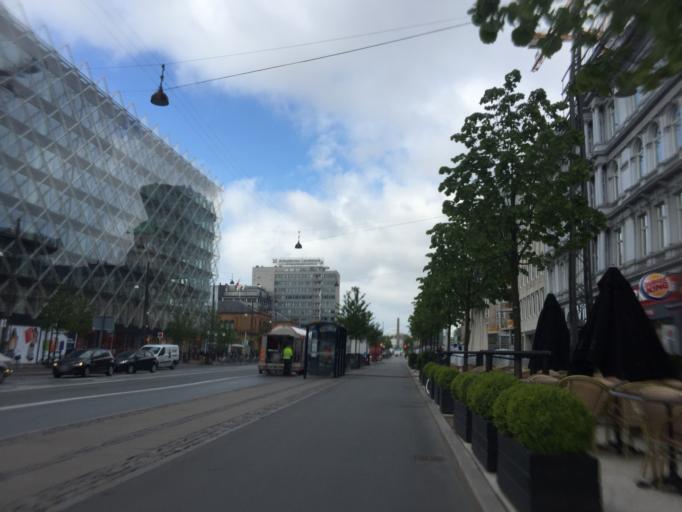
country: DK
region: Capital Region
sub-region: Kobenhavn
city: Copenhagen
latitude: 55.6757
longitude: 12.5673
